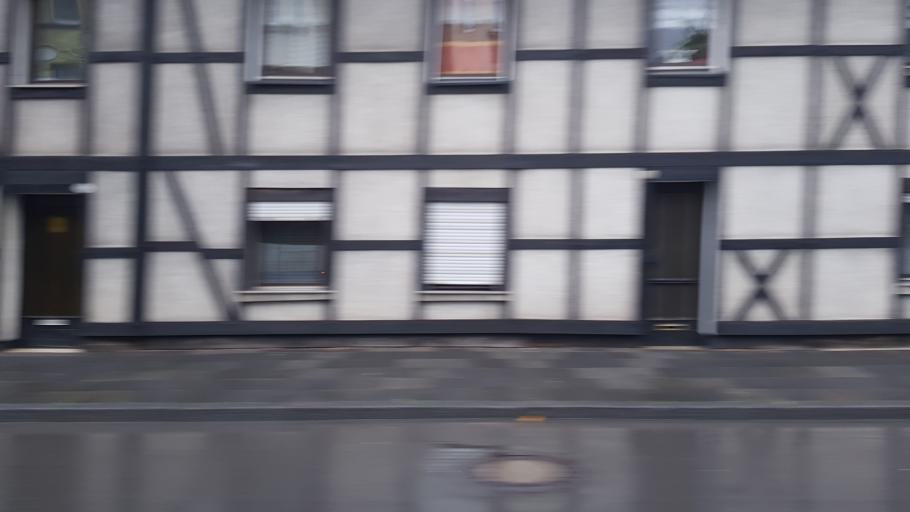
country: DE
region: North Rhine-Westphalia
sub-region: Regierungsbezirk Arnsberg
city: Hagen
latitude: 51.3484
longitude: 7.4868
